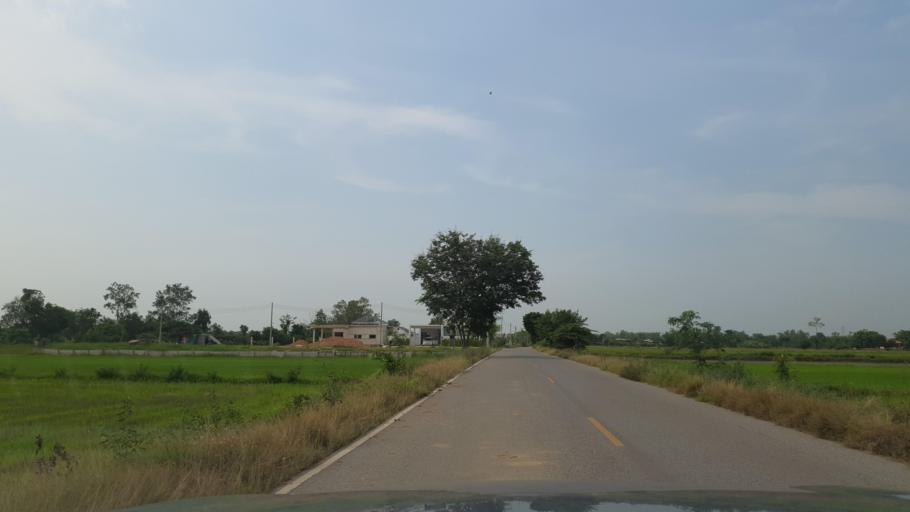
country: TH
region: Phitsanulok
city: Bang Rakam
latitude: 16.8051
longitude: 100.1626
